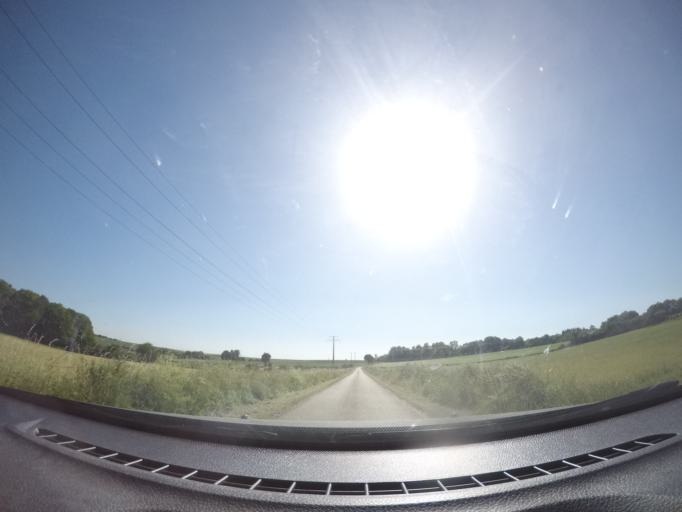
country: BE
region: Wallonia
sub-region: Province de Namur
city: Philippeville
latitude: 50.1852
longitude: 4.5954
